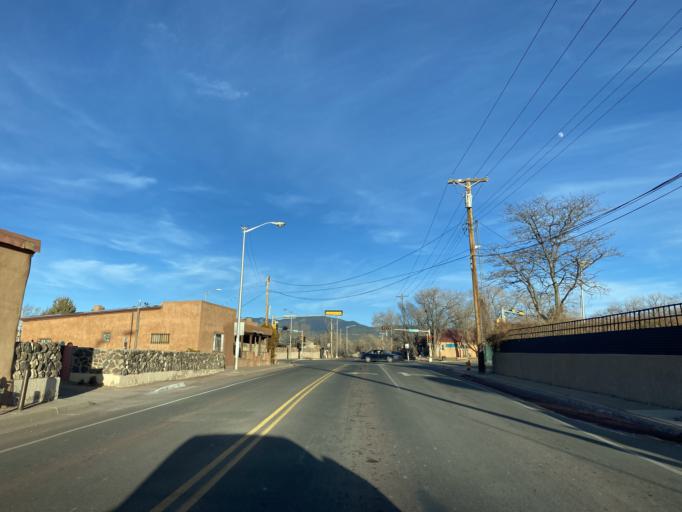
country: US
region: New Mexico
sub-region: Santa Fe County
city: Santa Fe
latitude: 35.6840
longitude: -105.9557
